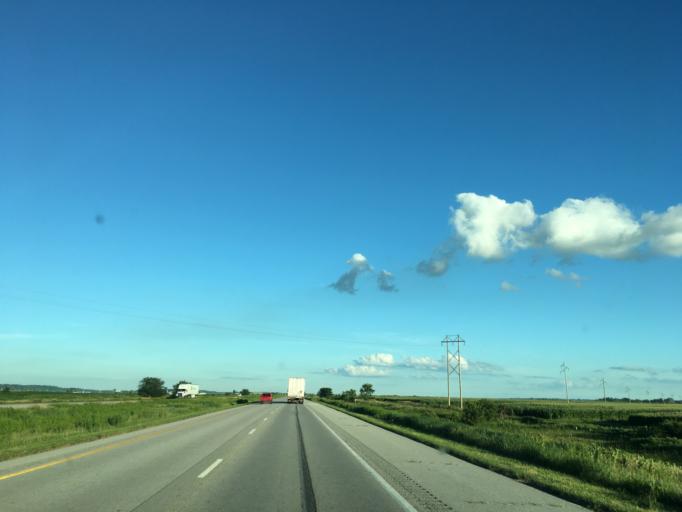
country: US
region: Nebraska
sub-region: Otoe County
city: Nebraska City
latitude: 40.6589
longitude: -95.7563
